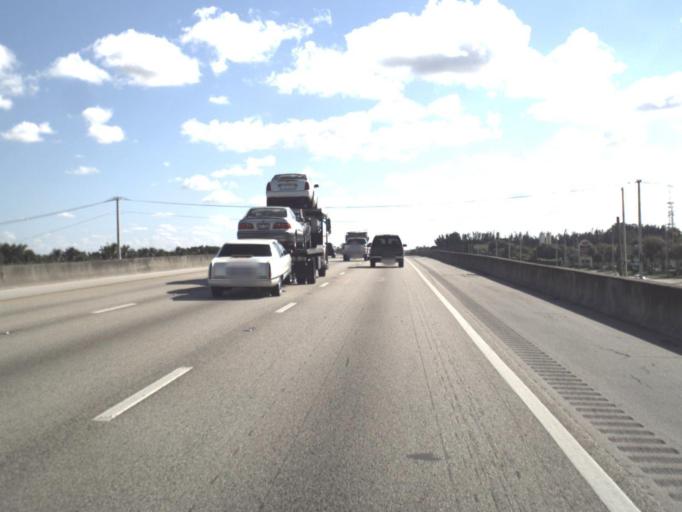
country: US
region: Florida
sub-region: Palm Beach County
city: Boca Del Mar
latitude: 26.3692
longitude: -80.1710
